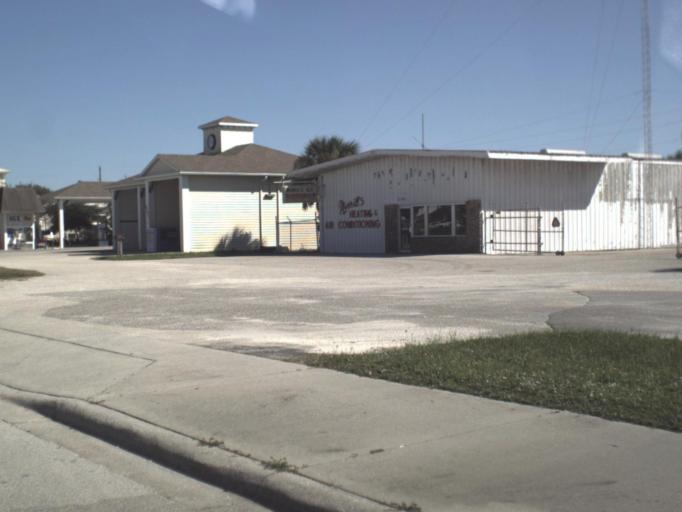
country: US
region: Florida
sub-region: Charlotte County
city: Grove City
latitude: 26.9345
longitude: -82.3145
